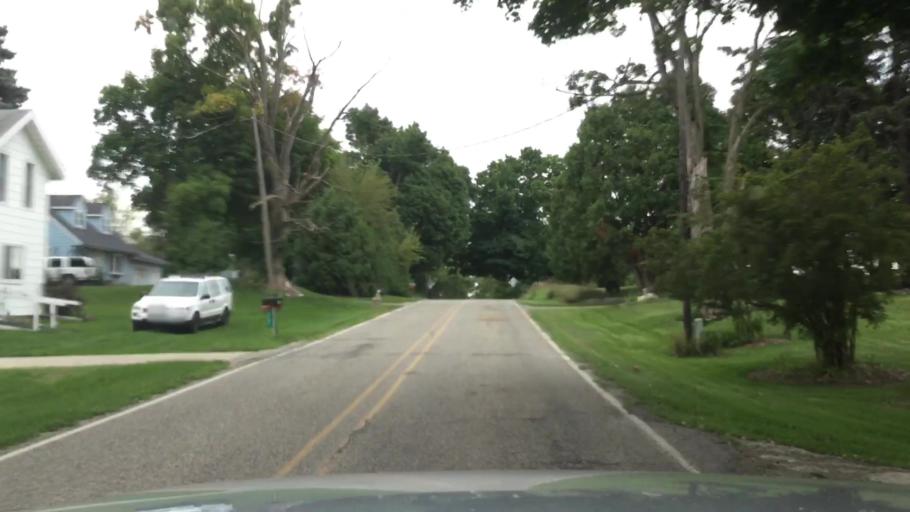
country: US
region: Michigan
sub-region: Shiawassee County
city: Durand
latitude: 42.9093
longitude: -84.0695
